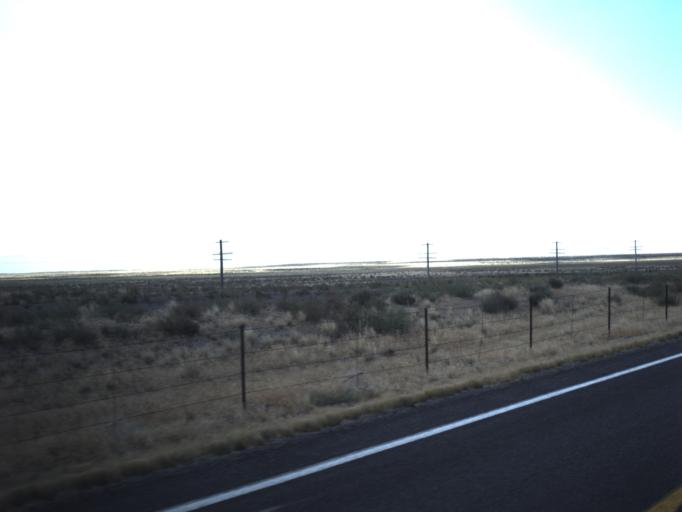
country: US
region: Utah
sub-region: Millard County
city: Delta
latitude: 38.9835
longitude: -112.7941
